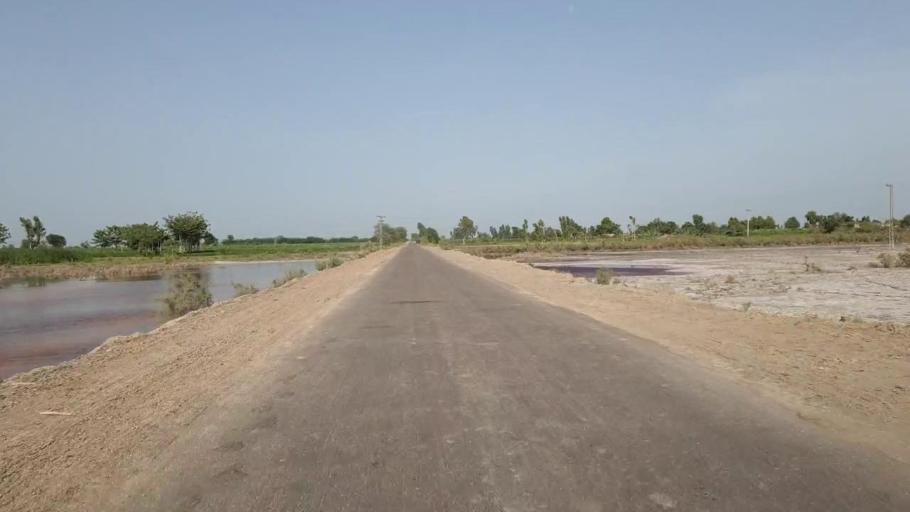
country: PK
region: Sindh
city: Sakrand
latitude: 26.2845
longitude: 68.2472
